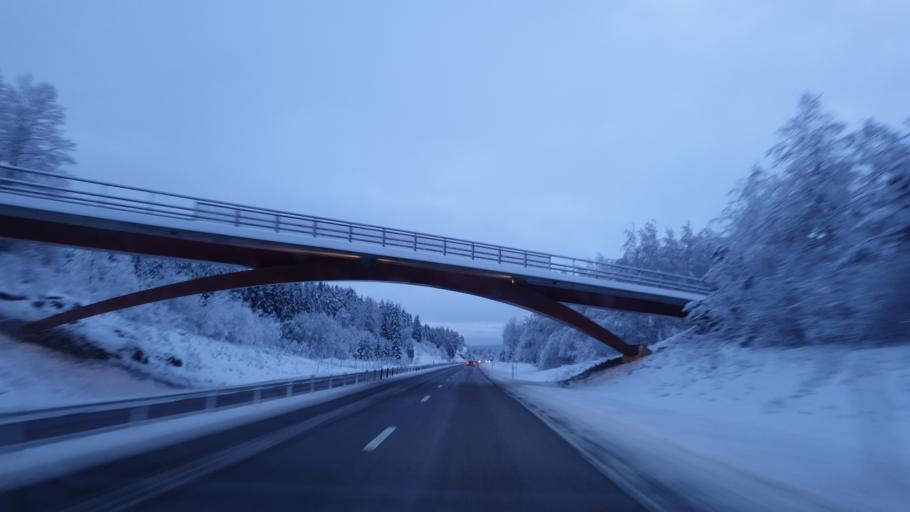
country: SE
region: Vaesternorrland
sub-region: Kramfors Kommun
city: Nordingra
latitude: 62.9352
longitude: 18.0938
